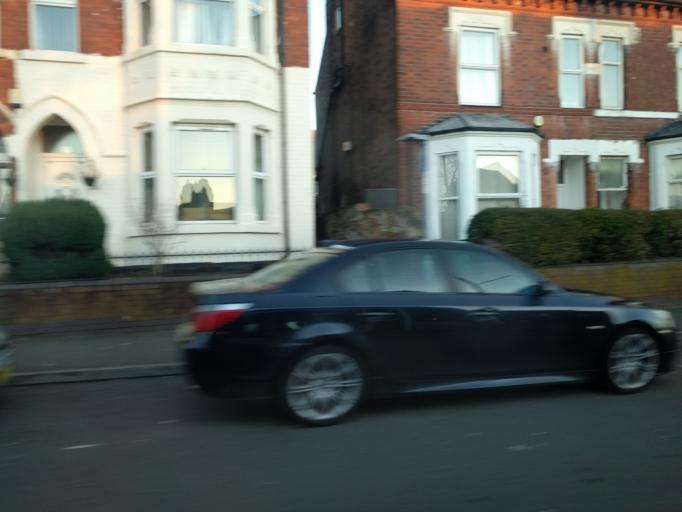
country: GB
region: England
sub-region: Nottingham
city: Nottingham
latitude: 52.9685
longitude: -1.1693
